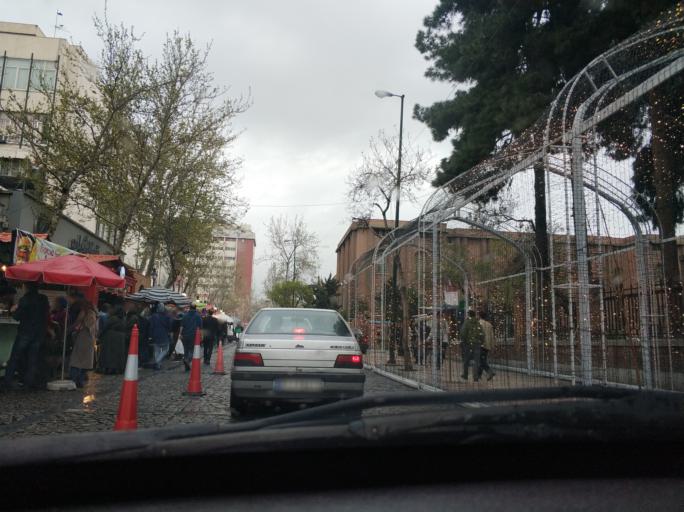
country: IR
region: Tehran
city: Tehran
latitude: 35.6862
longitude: 51.4143
